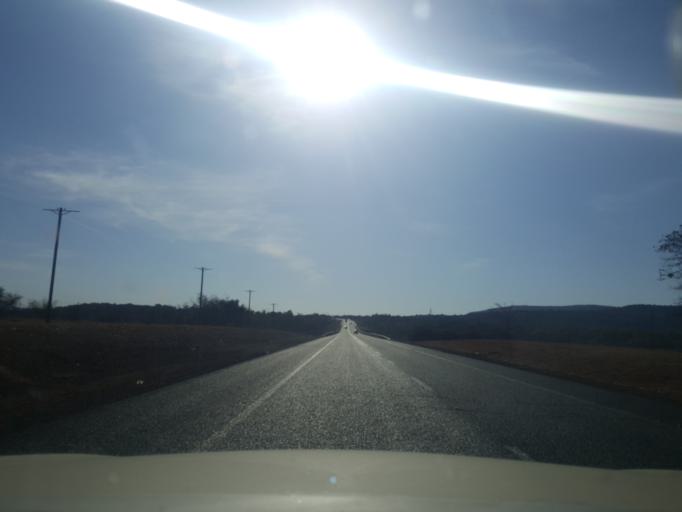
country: ZA
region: North-West
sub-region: Ngaka Modiri Molema District Municipality
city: Zeerust
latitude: -25.5470
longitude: 26.0514
